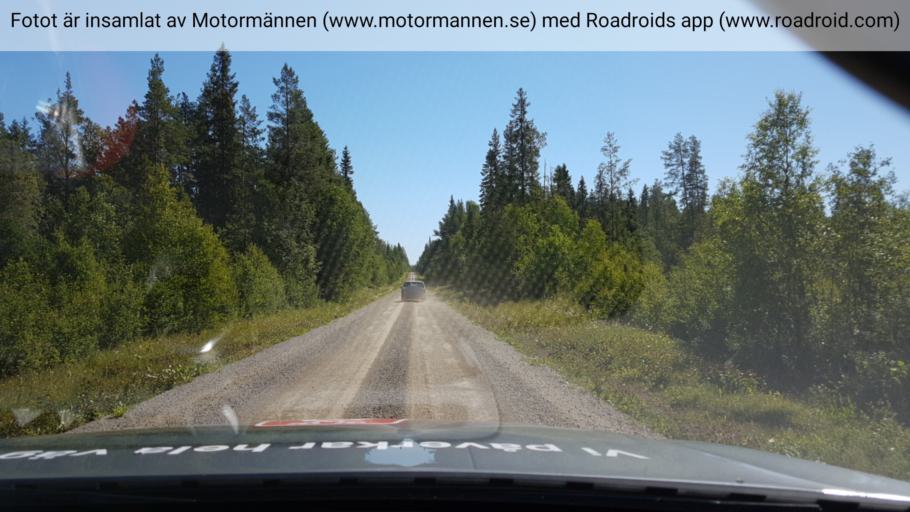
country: SE
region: Jaemtland
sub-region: Braecke Kommun
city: Braecke
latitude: 62.8013
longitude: 15.2381
